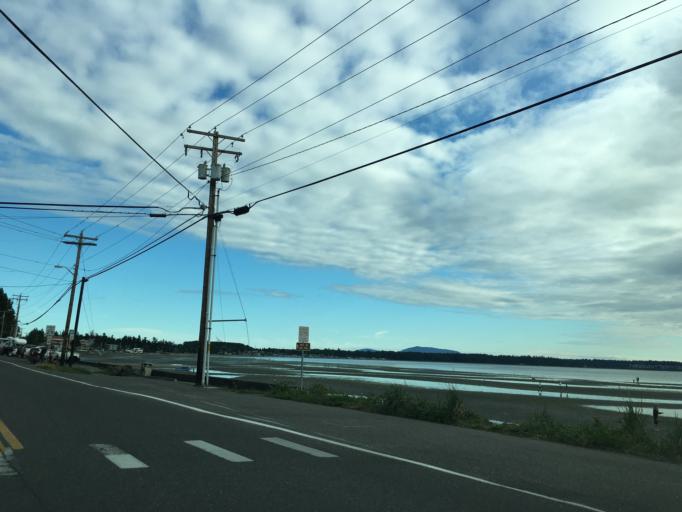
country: US
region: Washington
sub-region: Whatcom County
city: Birch Bay
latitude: 48.9339
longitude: -122.7485
